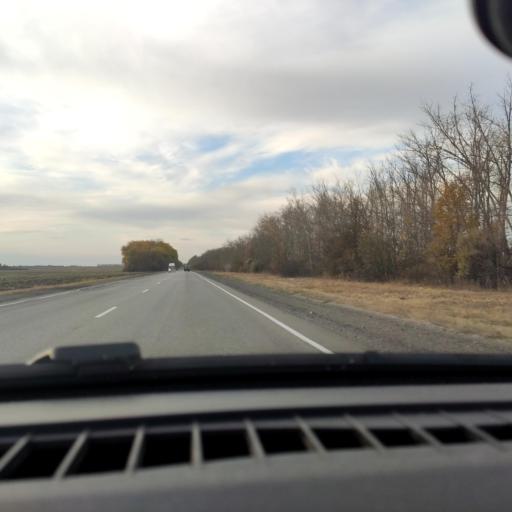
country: RU
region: Voronezj
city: Ostrogozhsk
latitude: 50.9532
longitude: 39.0416
